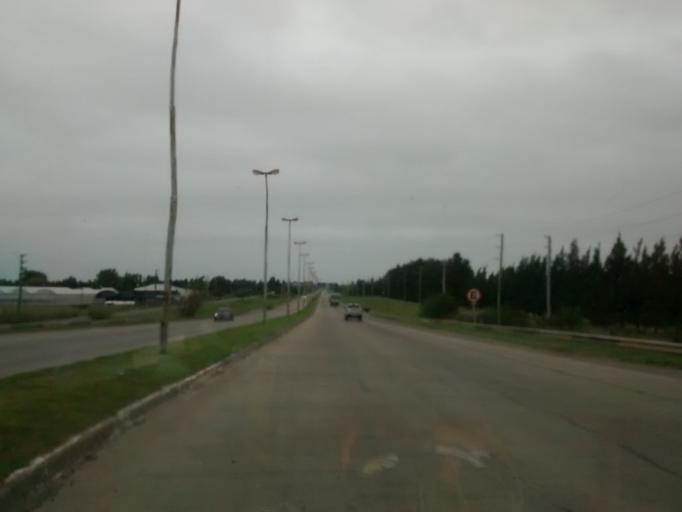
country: AR
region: Buenos Aires
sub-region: Partido de La Plata
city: La Plata
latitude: -35.0371
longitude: -58.0943
